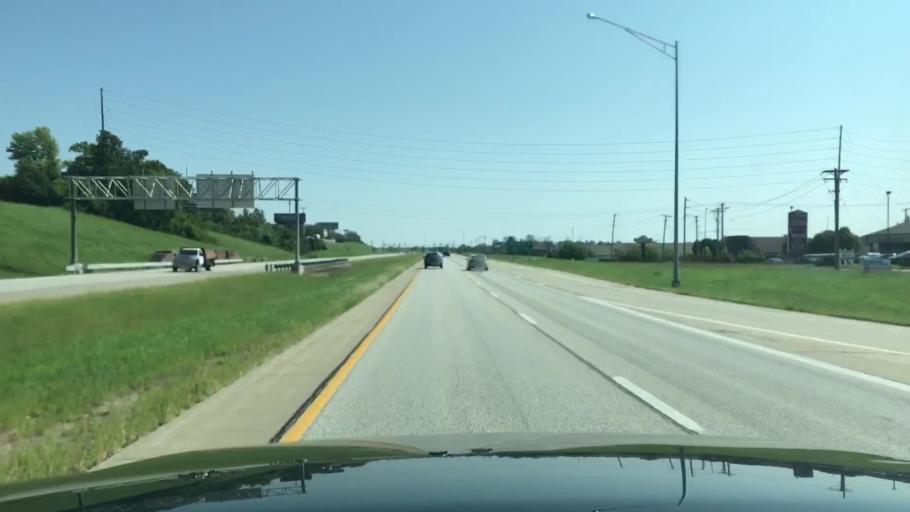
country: US
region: Missouri
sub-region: Saint Charles County
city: Saint Charles
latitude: 38.7573
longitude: -90.5407
